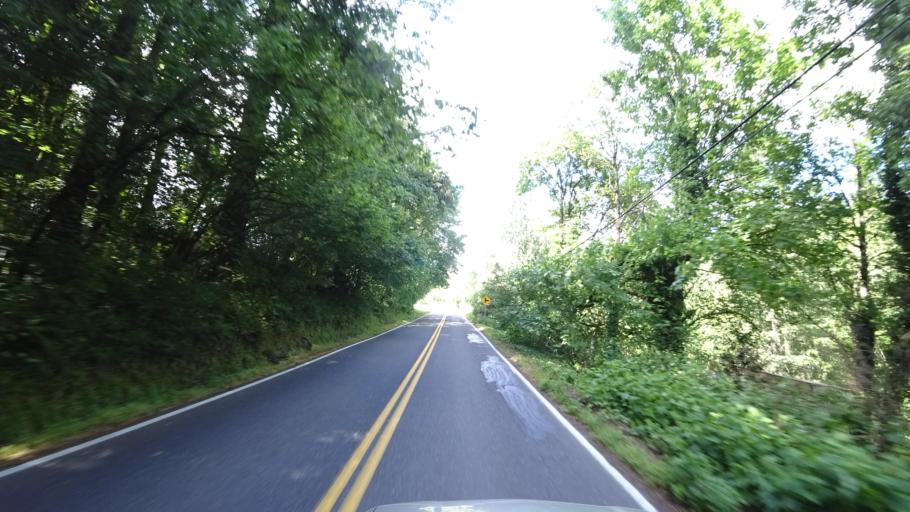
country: US
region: Oregon
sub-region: Washington County
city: Bethany
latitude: 45.6045
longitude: -122.8330
